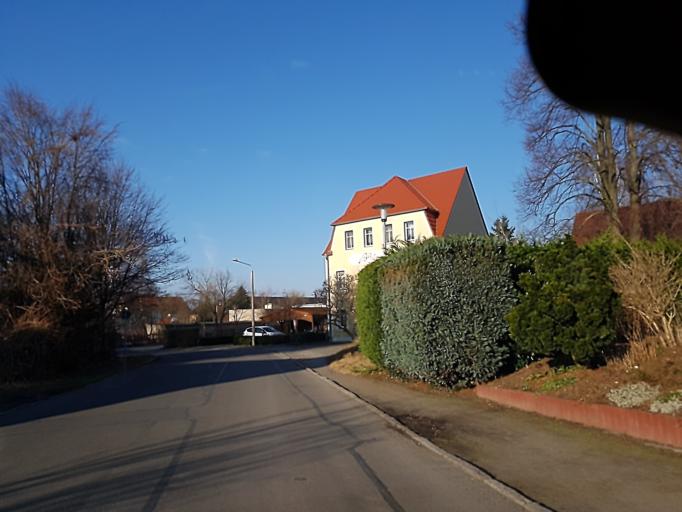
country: DE
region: Brandenburg
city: Bad Liebenwerda
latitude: 51.5120
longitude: 13.3952
